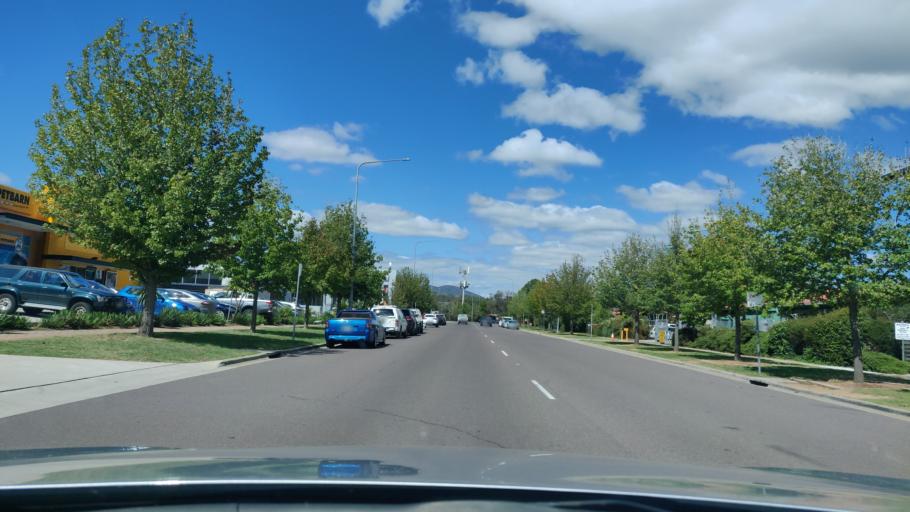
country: AU
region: Australian Capital Territory
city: Macarthur
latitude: -35.4220
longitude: 149.0693
